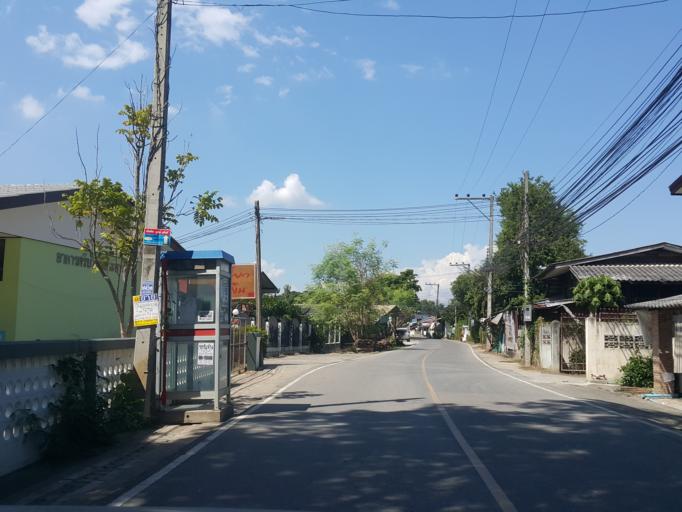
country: TH
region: Chiang Mai
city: Saraphi
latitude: 18.7696
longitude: 99.0433
